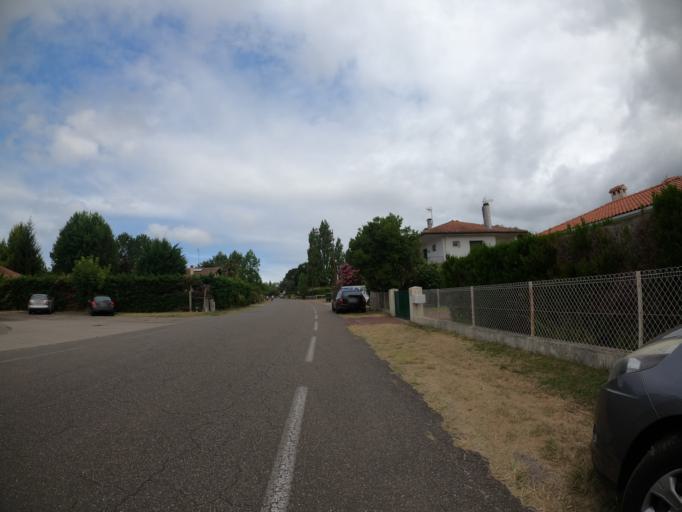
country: FR
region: Aquitaine
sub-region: Departement des Landes
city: Leon
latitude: 43.8784
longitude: -1.3032
